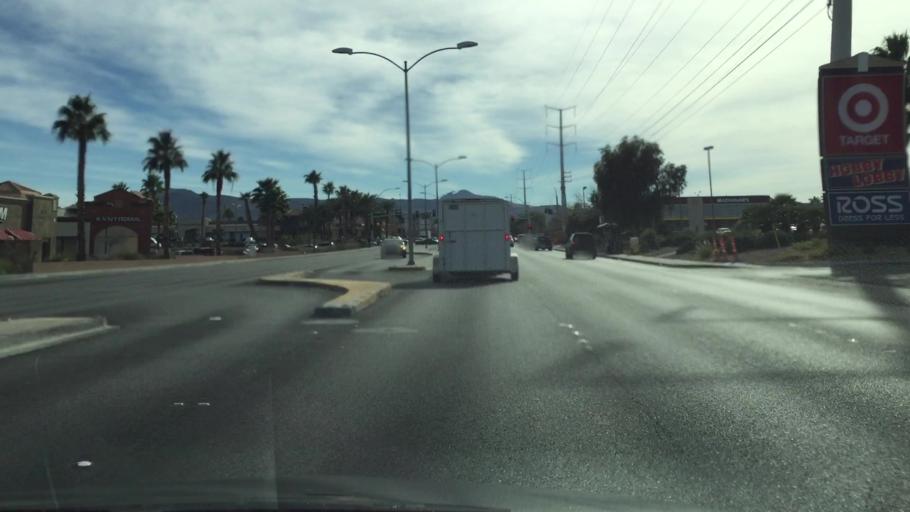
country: US
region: Nevada
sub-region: Clark County
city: Whitney
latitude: 36.0655
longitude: -115.0462
